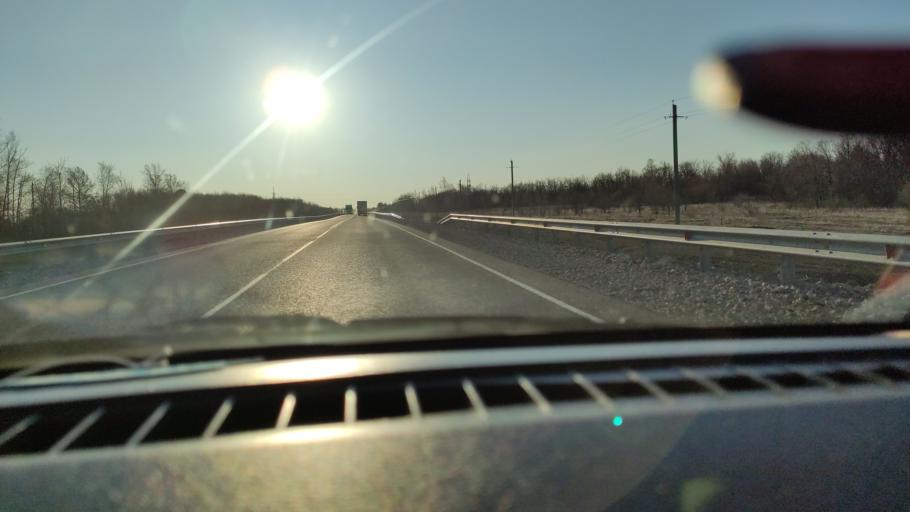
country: RU
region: Saratov
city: Shikhany
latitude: 52.1613
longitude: 47.1554
